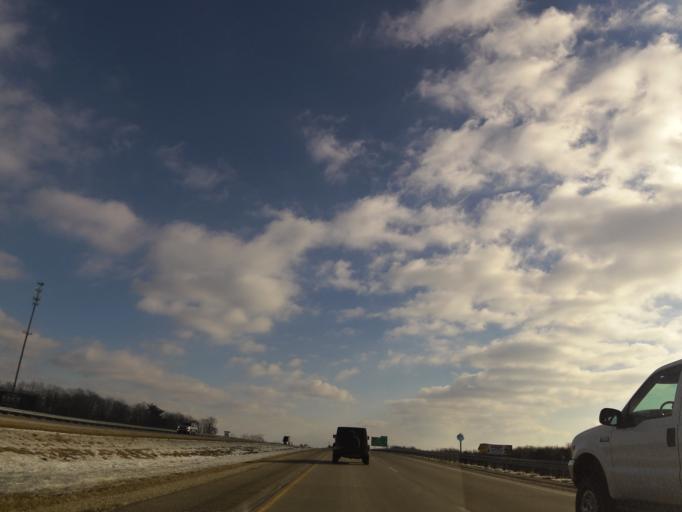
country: US
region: Wisconsin
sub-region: Juneau County
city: New Lisbon
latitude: 43.8868
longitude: -90.1550
